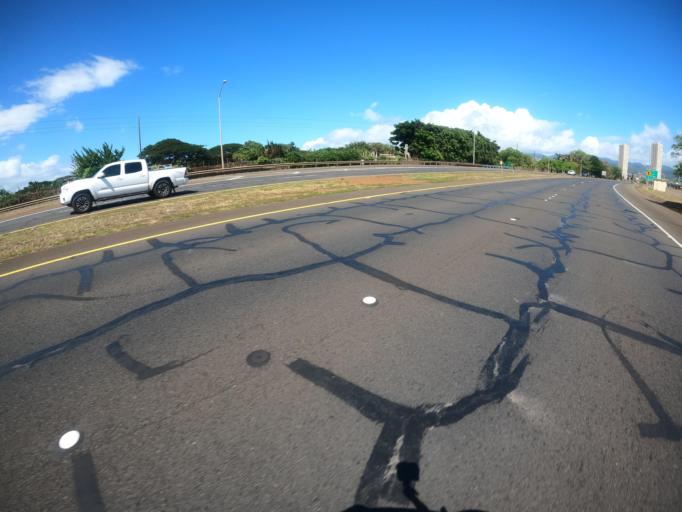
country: US
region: Hawaii
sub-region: Honolulu County
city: Pearl City, Manana
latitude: 21.3948
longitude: -157.9874
